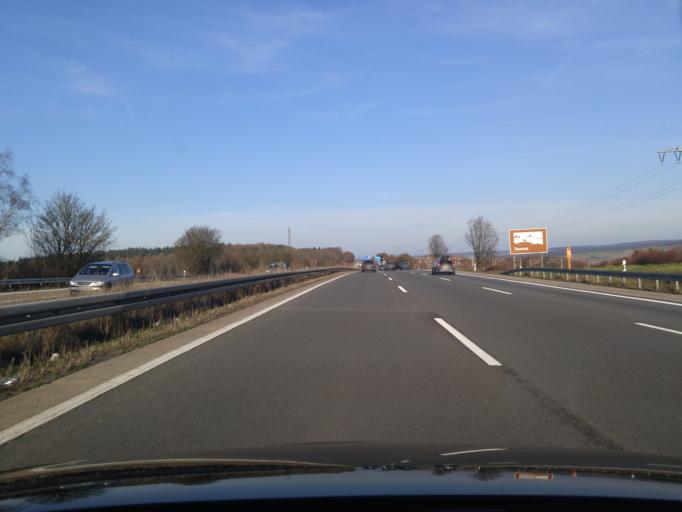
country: DE
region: Hesse
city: Bad Camberg
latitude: 50.2807
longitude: 8.2409
